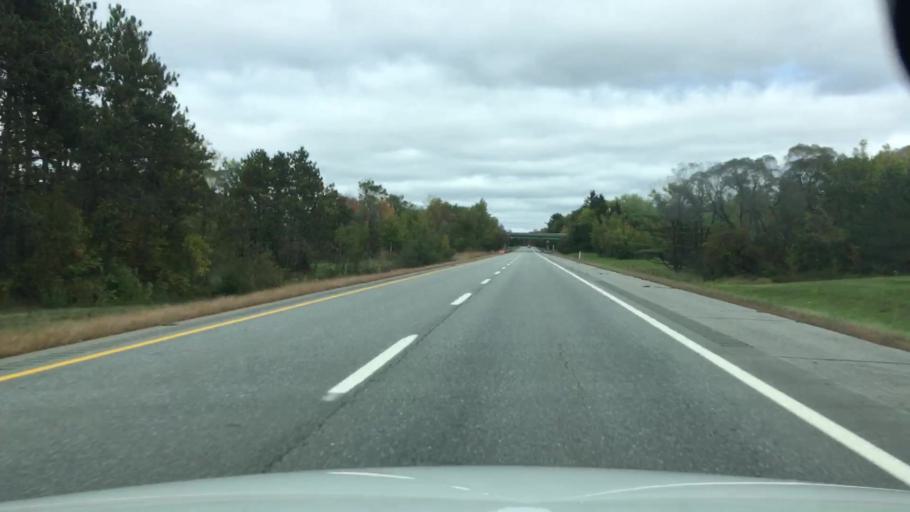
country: US
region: Maine
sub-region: Kennebec County
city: Clinton
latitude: 44.6591
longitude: -69.5014
